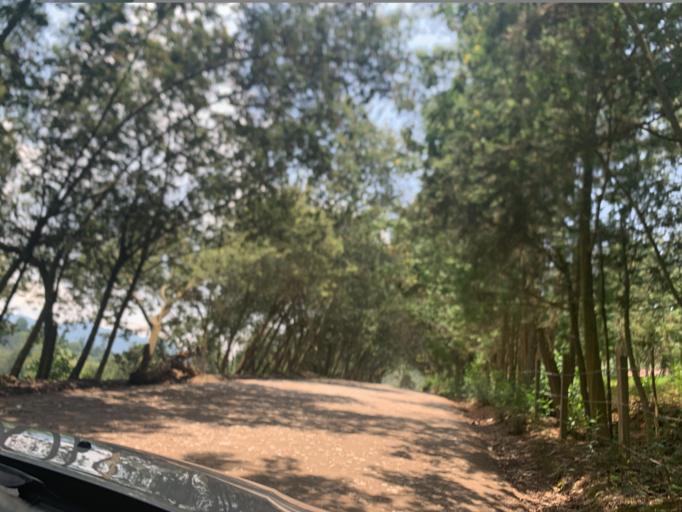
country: CO
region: Boyaca
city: Chiquinquira
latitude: 5.5873
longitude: -73.7477
